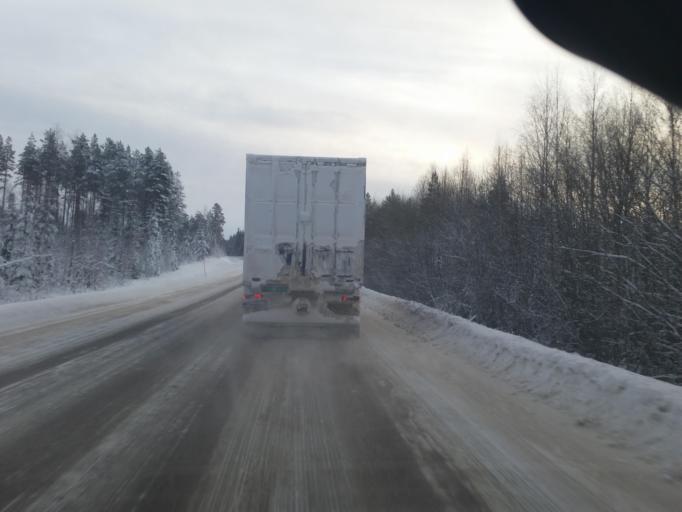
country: SE
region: Norrbotten
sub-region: Alvsbyns Kommun
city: AElvsbyn
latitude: 65.6503
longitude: 21.2380
